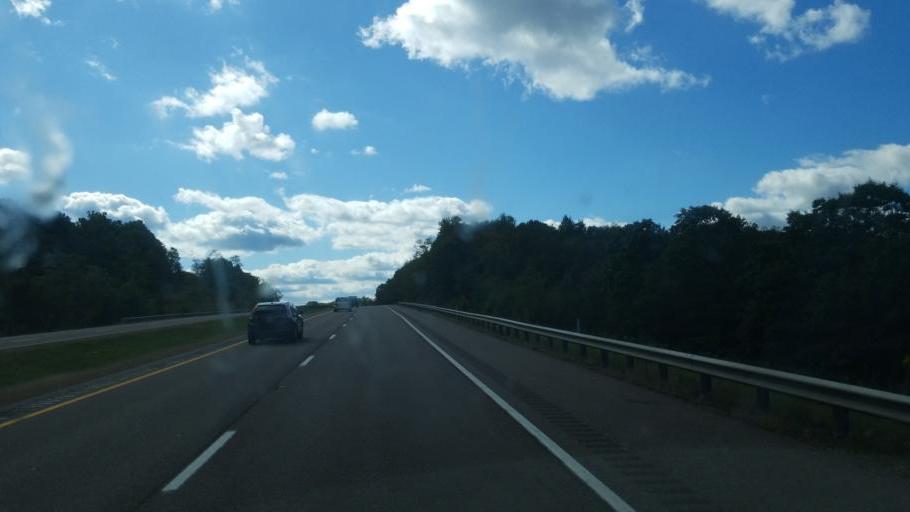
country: US
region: Maryland
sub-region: Garrett County
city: Oakland
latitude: 39.6967
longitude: -79.3346
